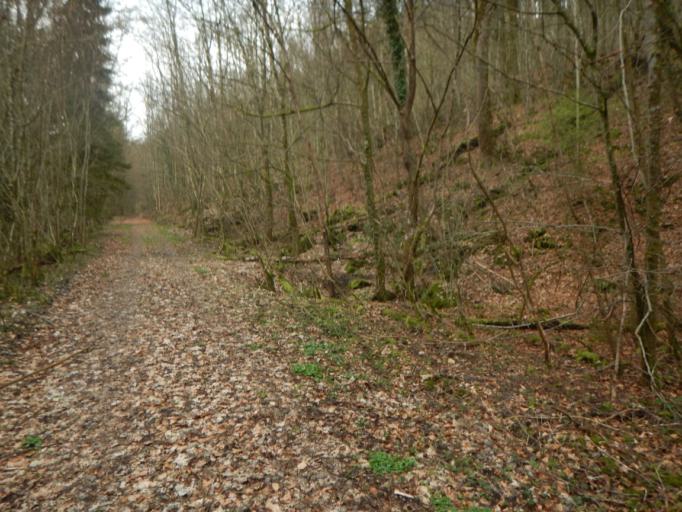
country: LU
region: Grevenmacher
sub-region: Canton d'Echternach
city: Beaufort
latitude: 49.8411
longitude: 6.3169
